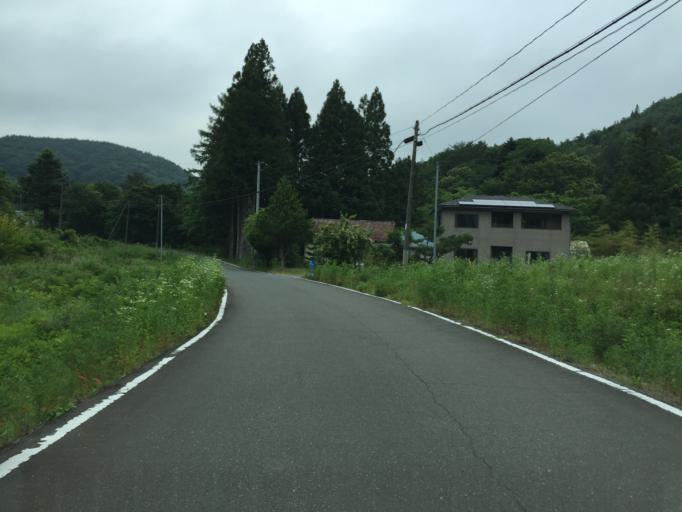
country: JP
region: Fukushima
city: Yanagawamachi-saiwaicho
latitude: 37.7884
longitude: 140.7170
